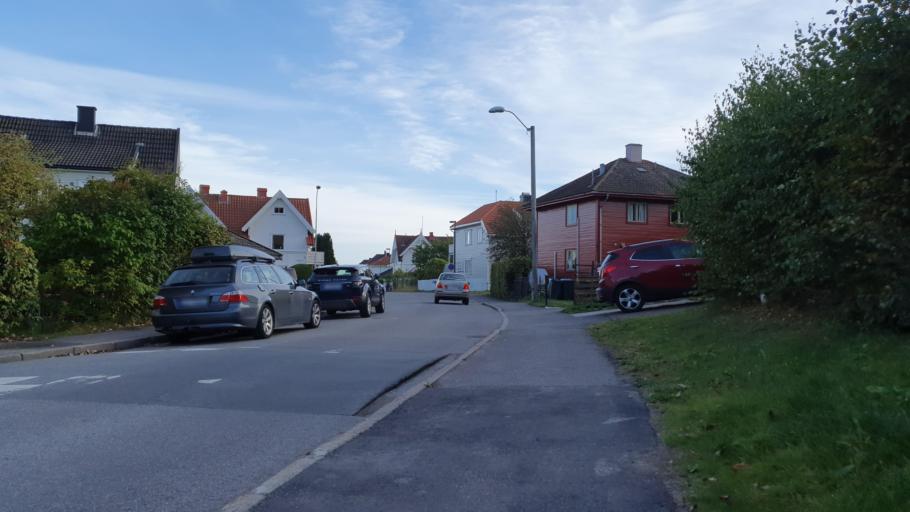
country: NO
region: Vestfold
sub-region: Tonsberg
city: Tonsberg
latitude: 59.2698
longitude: 10.4231
